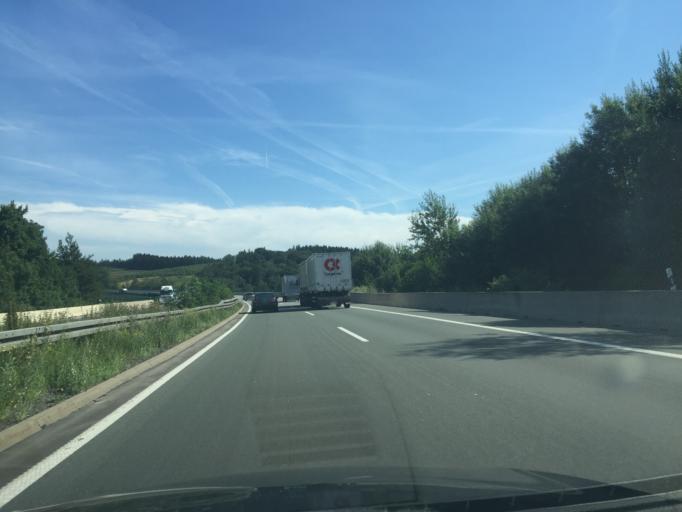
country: DE
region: North Rhine-Westphalia
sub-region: Regierungsbezirk Arnsberg
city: Drolshagen
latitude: 51.0578
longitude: 7.7224
